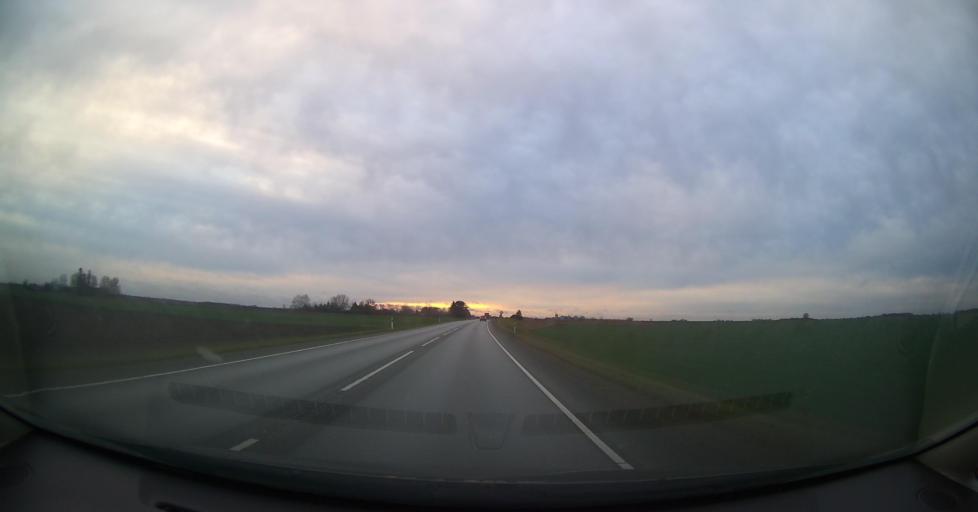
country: EE
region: Ida-Virumaa
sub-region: Kohtla-Nomme vald
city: Kohtla-Nomme
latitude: 59.4117
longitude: 27.1277
